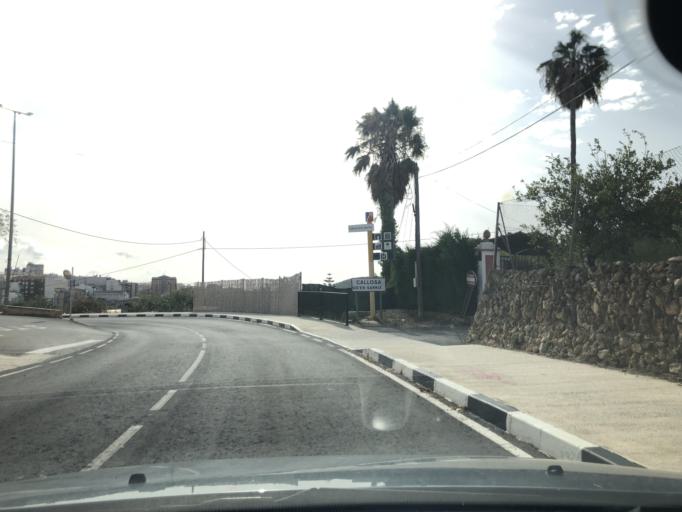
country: ES
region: Valencia
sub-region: Provincia de Alicante
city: Callosa d'En Sarria
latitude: 38.6513
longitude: -0.1306
